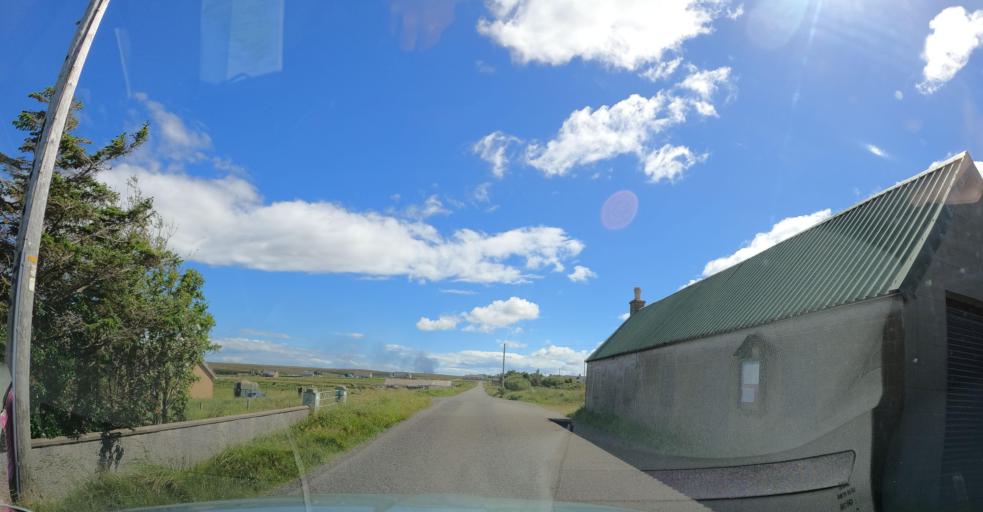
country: GB
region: Scotland
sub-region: Eilean Siar
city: Isle of Lewis
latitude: 58.3510
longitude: -6.5465
